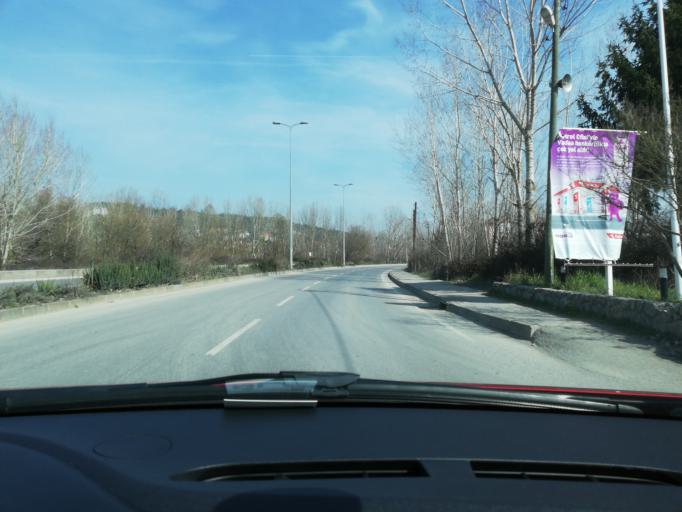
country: TR
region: Bartin
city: Bartin
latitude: 41.6351
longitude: 32.3486
